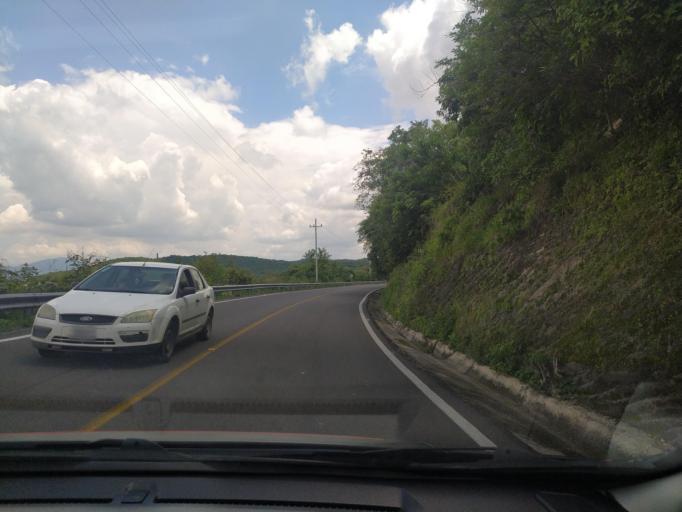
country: MX
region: Jalisco
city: Villa Corona
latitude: 20.3924
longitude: -103.6744
